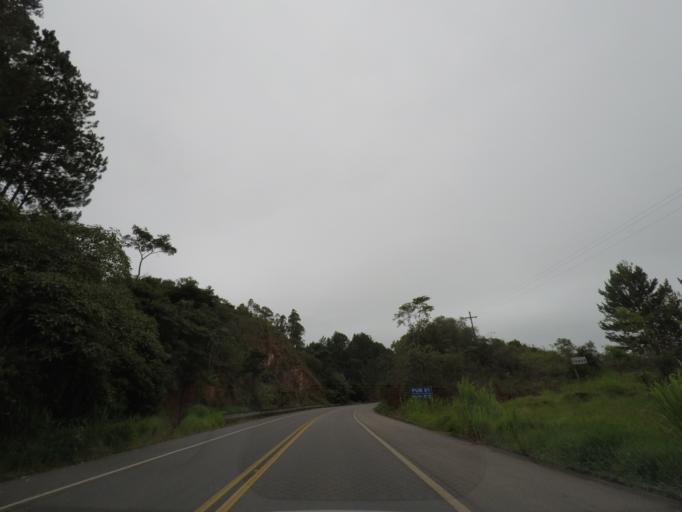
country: BR
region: Sao Paulo
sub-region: Cunha
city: Cunha
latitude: -23.0732
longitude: -44.9664
